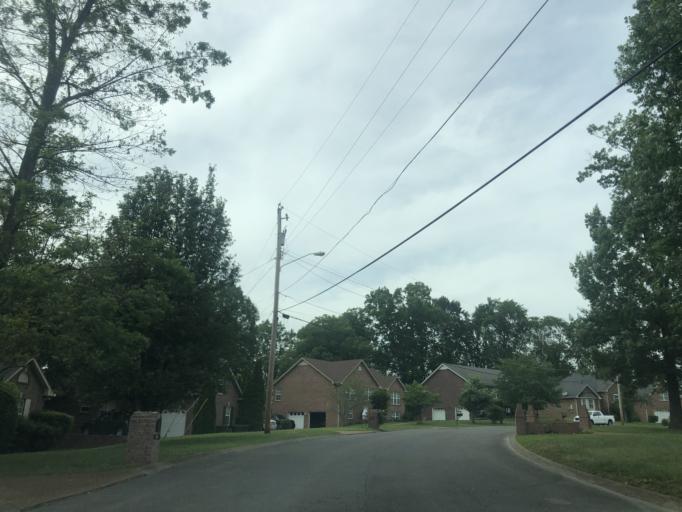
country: US
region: Tennessee
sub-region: Davidson County
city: Nashville
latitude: 36.2094
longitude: -86.8097
